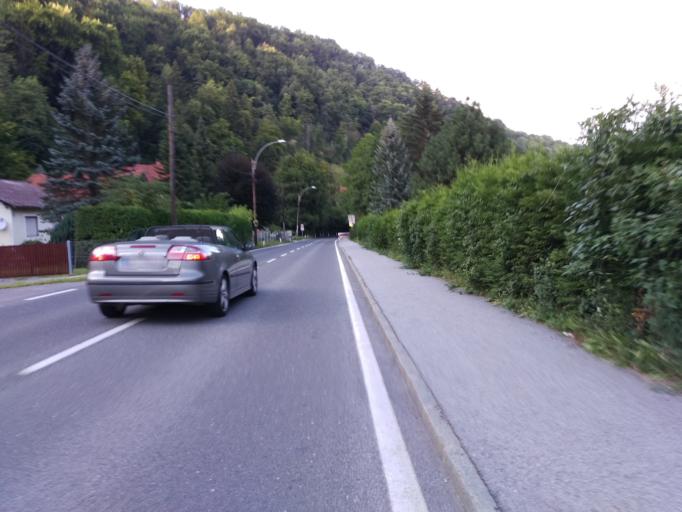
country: AT
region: Styria
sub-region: Politischer Bezirk Graz-Umgebung
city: Thal
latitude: 47.0574
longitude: 15.3750
